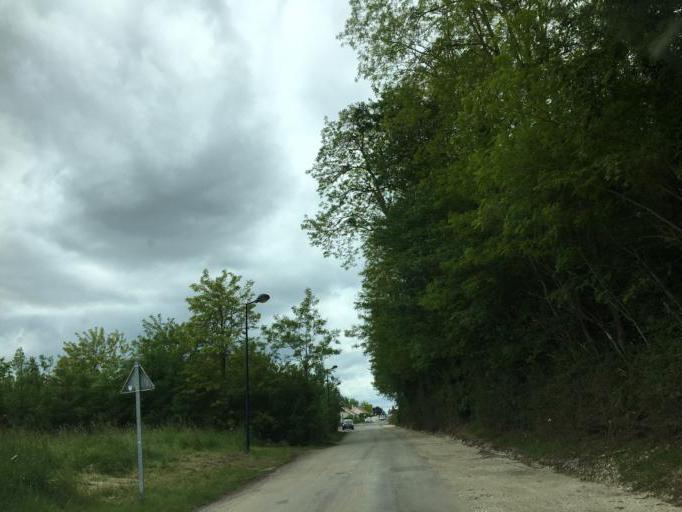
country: FR
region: Centre
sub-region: Departement du Loiret
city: Semoy
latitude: 47.9408
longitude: 1.9474
